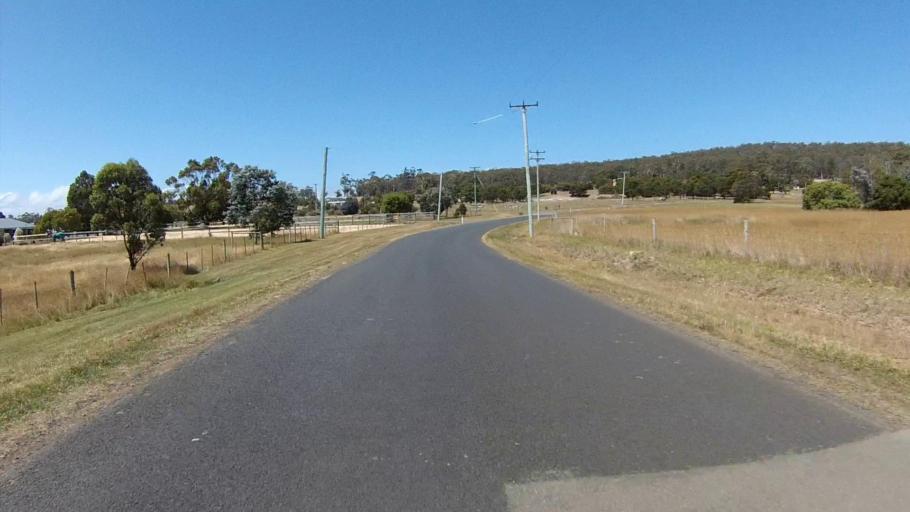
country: AU
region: Tasmania
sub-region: Clarence
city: Sandford
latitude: -42.9568
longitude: 147.4805
